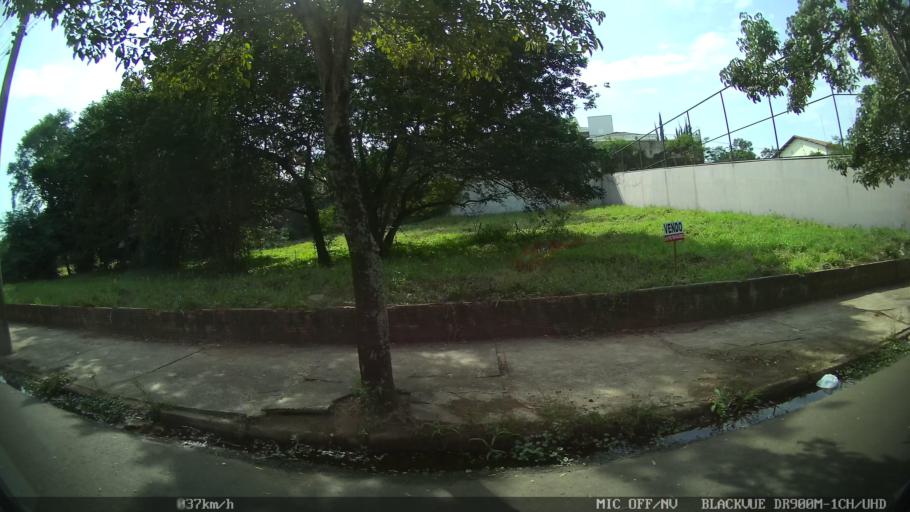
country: BR
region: Sao Paulo
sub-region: Piracicaba
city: Piracicaba
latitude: -22.7239
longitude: -47.6677
